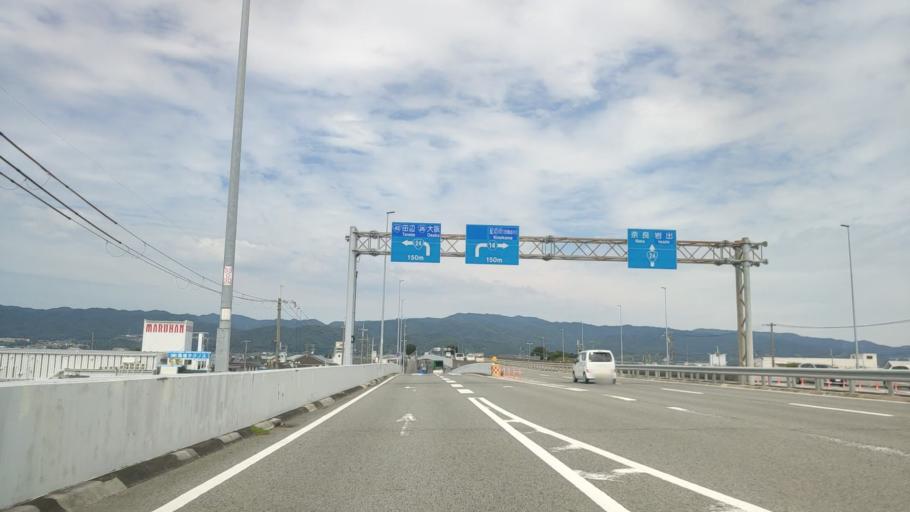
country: JP
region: Wakayama
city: Wakayama-shi
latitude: 34.2432
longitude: 135.2176
